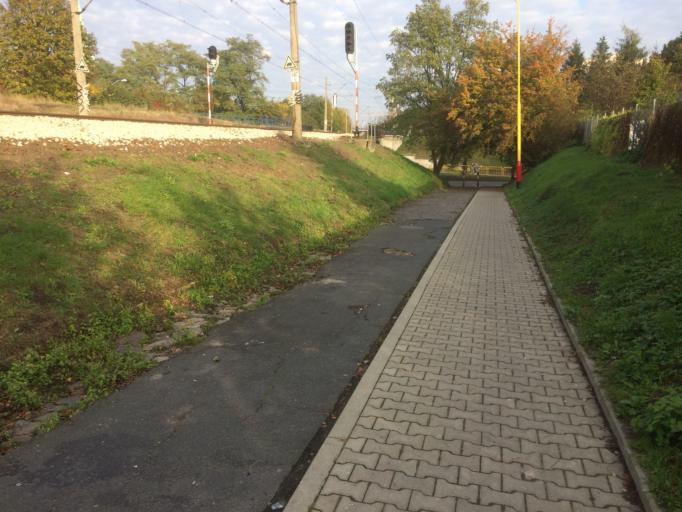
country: PL
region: Lubusz
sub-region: Powiat swiebodzinski
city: Swiebodzin
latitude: 52.2435
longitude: 15.5319
